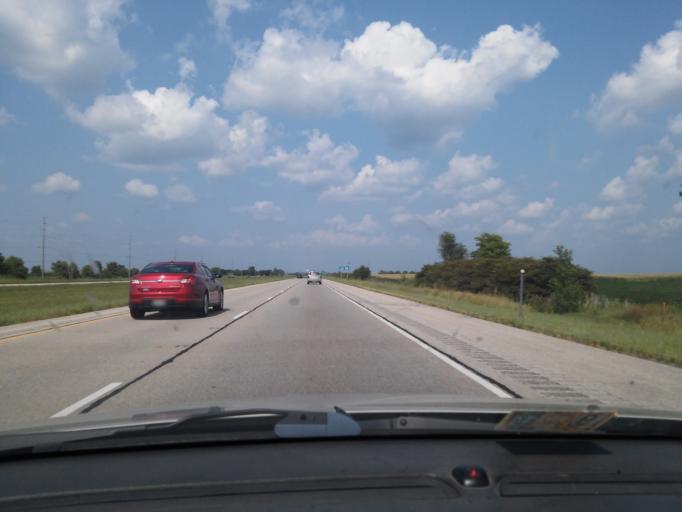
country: US
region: Illinois
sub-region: Logan County
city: Atlanta
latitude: 40.2956
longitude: -89.1904
